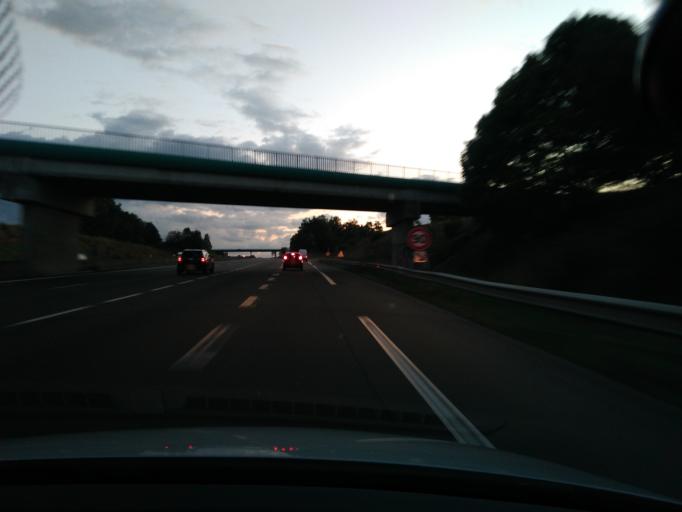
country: FR
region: Ile-de-France
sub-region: Departement de Seine-et-Marne
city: Saint-Germain-sur-Morin
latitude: 48.8638
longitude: 2.8480
